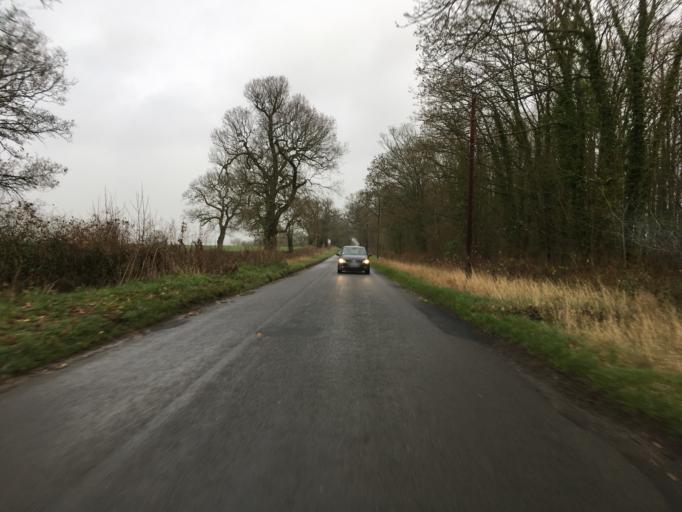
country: GB
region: England
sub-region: Wiltshire
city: Luckington
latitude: 51.5337
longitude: -2.2111
